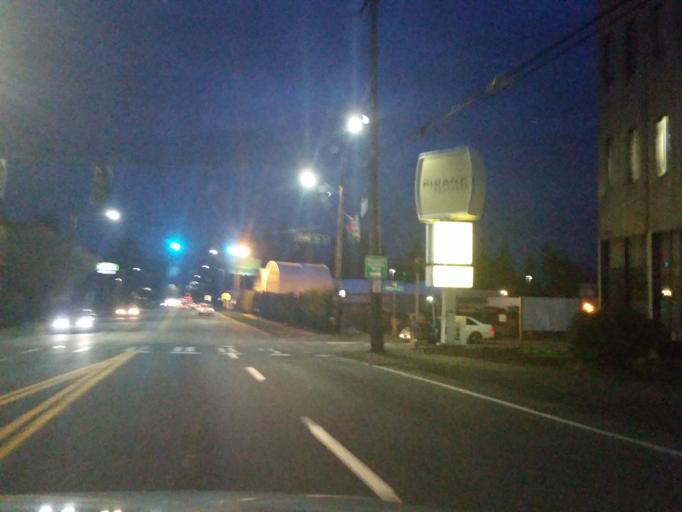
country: US
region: Washington
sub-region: King County
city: Shoreline
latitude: 47.7233
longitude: -122.3428
